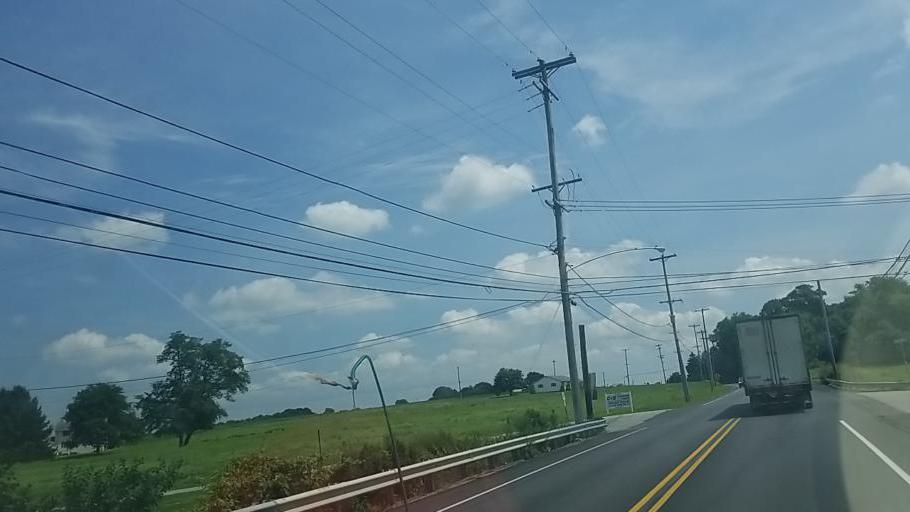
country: US
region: Pennsylvania
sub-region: Chester County
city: Toughkenamon
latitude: 39.8028
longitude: -75.7401
